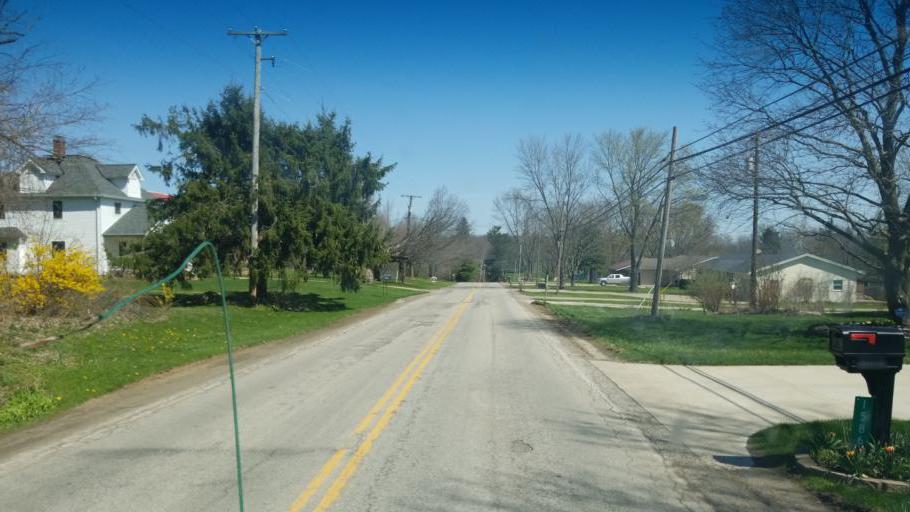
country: US
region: Ohio
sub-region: Richland County
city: Lincoln Heights
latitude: 40.7981
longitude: -82.4441
